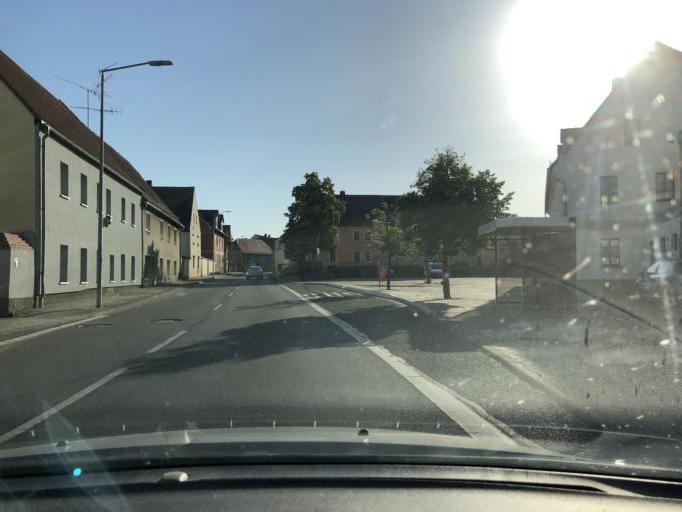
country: DE
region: Saxony
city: Dahlen
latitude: 51.3282
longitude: 13.0068
